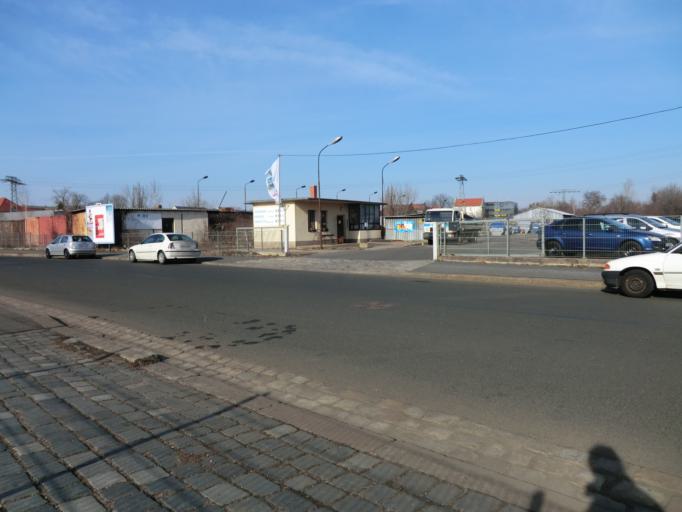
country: DE
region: Saxony
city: Dresden
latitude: 51.0460
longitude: 13.7106
